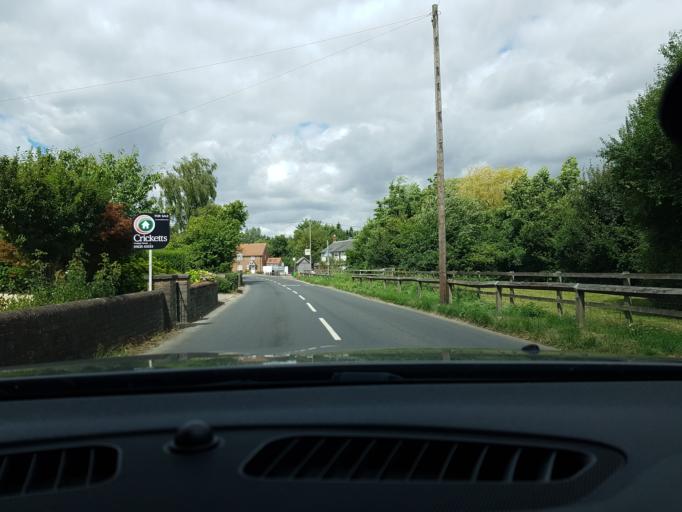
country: GB
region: England
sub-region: West Berkshire
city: Wickham
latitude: 51.4736
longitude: -1.4480
